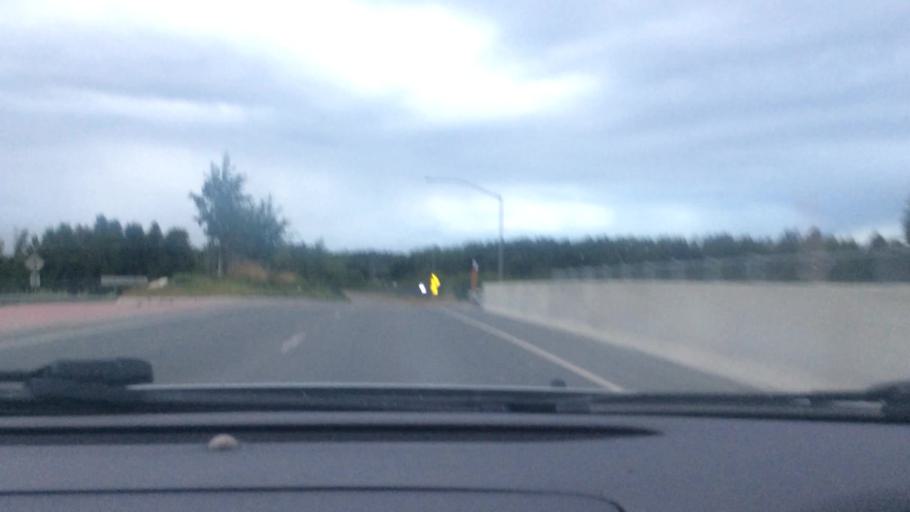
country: US
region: Alaska
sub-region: Anchorage Municipality
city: Anchorage
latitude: 61.1780
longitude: -149.7958
